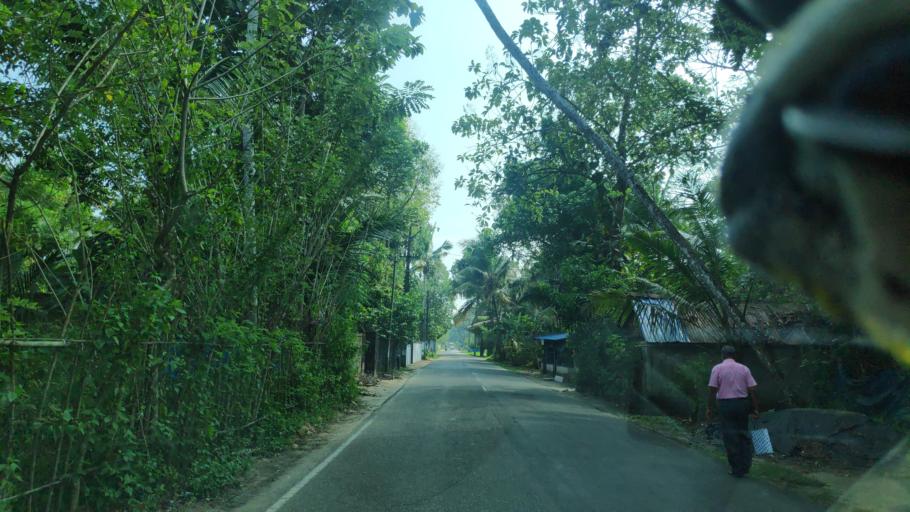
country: IN
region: Kerala
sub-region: Alappuzha
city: Shertallai
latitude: 9.6157
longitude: 76.3011
